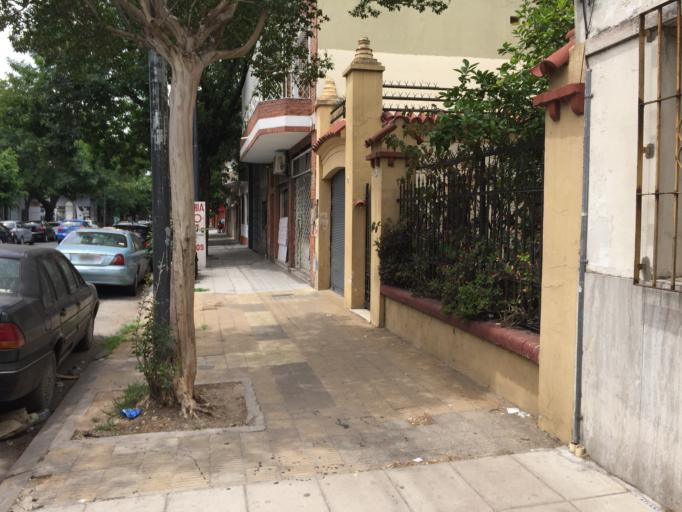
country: AR
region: Buenos Aires F.D.
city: Colegiales
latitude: -34.5894
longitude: -58.4448
